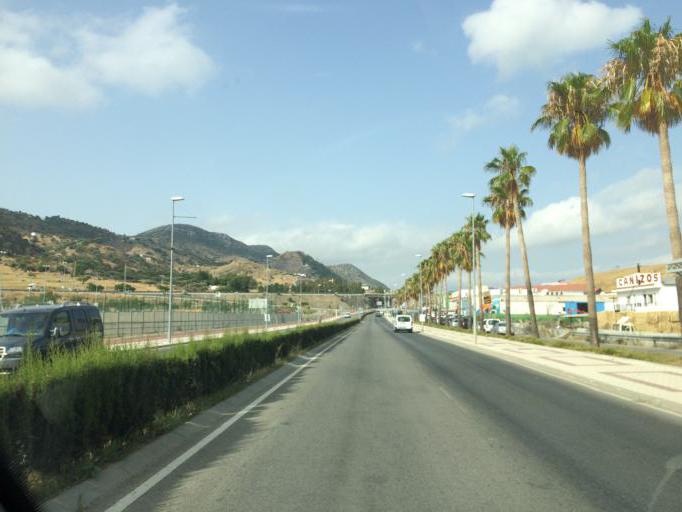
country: ES
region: Andalusia
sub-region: Provincia de Malaga
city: Estacion de Cartama
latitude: 36.7208
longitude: -4.6174
